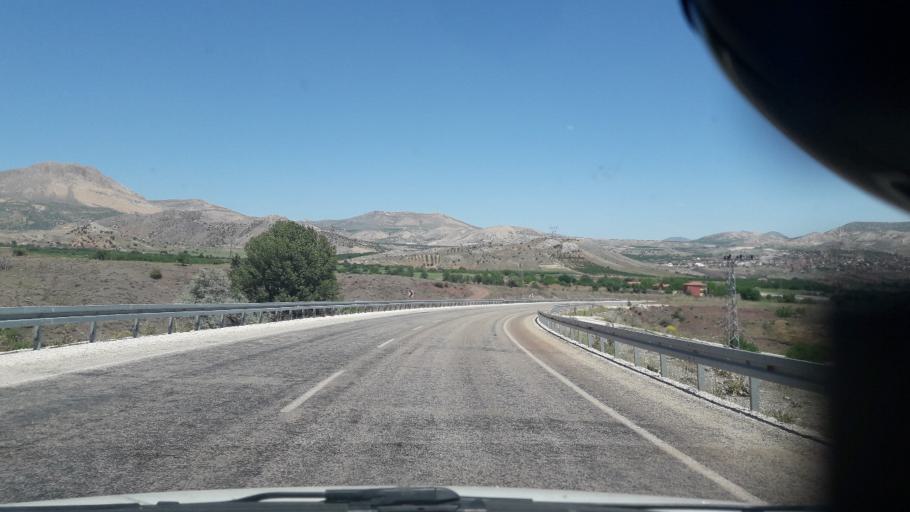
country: TR
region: Malatya
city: Hekimhan
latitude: 38.8222
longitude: 37.8855
